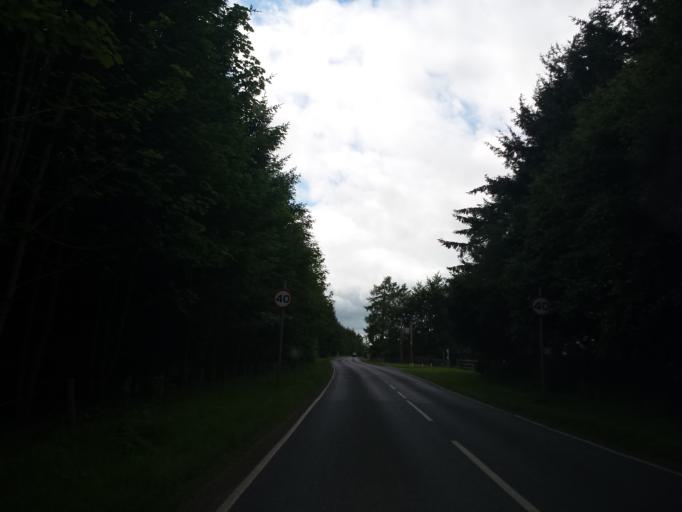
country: GB
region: Scotland
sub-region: Highland
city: Fortrose
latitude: 57.4859
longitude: -4.0564
